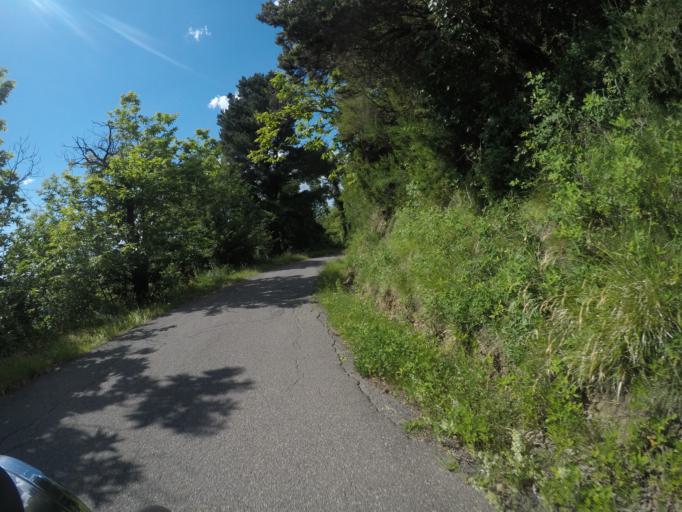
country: IT
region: Tuscany
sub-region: Provincia di Massa-Carrara
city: Casola in Lunigiana
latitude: 44.1773
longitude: 10.1643
